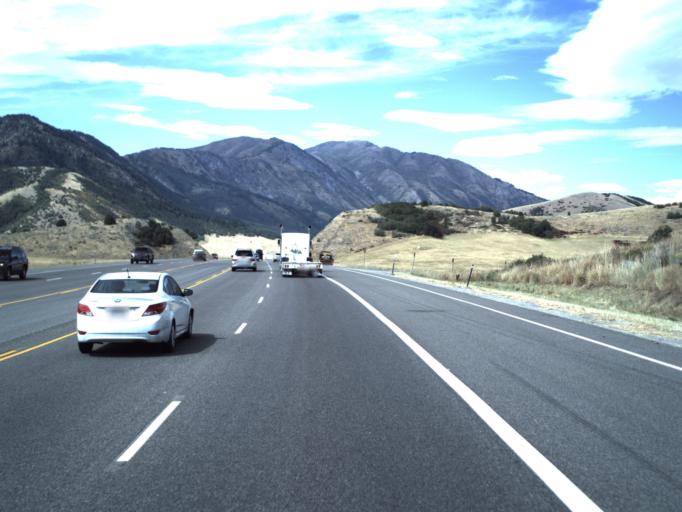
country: US
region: Utah
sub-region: Box Elder County
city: Brigham City
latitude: 41.5525
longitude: -111.9545
